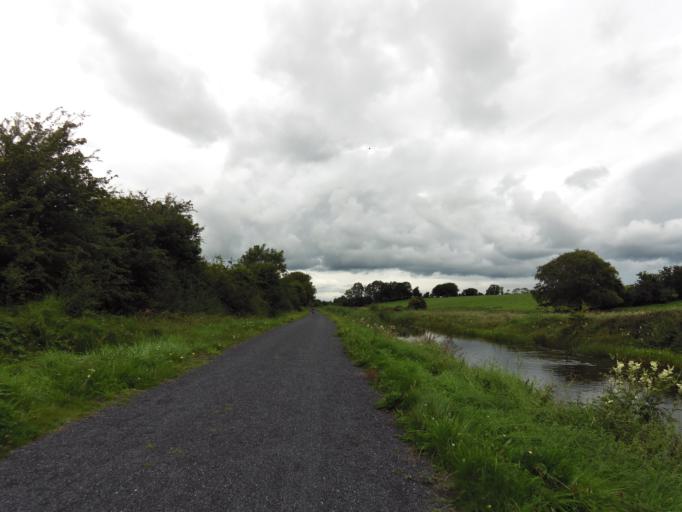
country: IE
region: Leinster
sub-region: An Iarmhi
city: An Muileann gCearr
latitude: 53.5165
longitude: -7.4324
